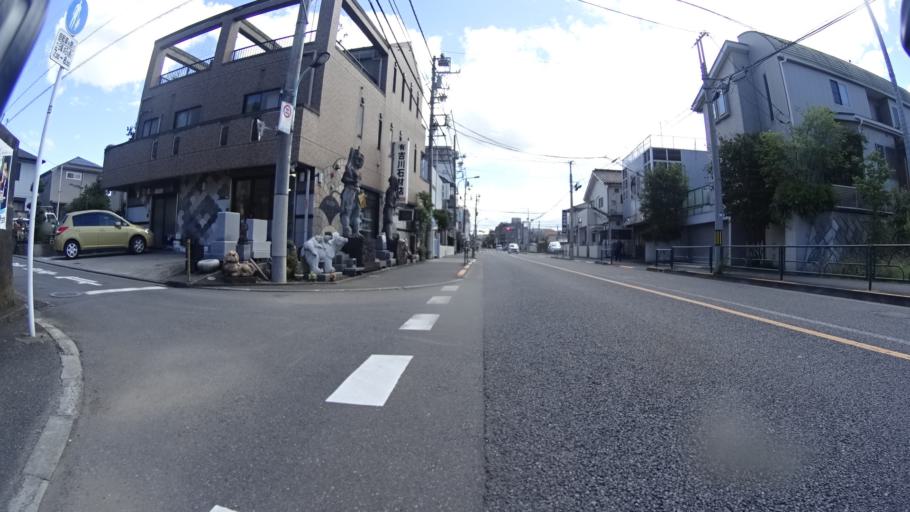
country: JP
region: Tokyo
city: Ome
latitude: 35.7922
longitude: 139.2707
